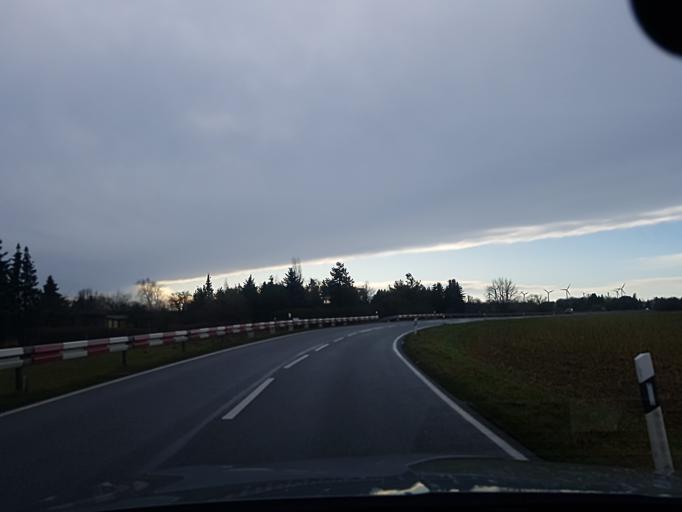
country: DE
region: Brandenburg
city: Falkenberg
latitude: 51.6034
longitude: 13.3118
